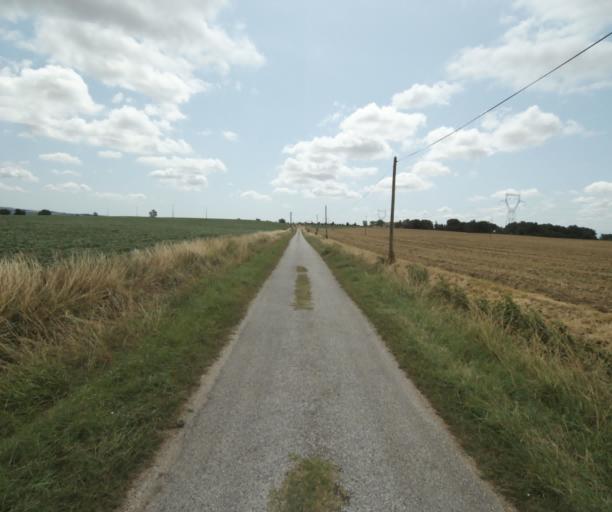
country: FR
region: Midi-Pyrenees
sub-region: Departement de la Haute-Garonne
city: Saint-Felix-Lauragais
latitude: 43.4204
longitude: 1.9028
